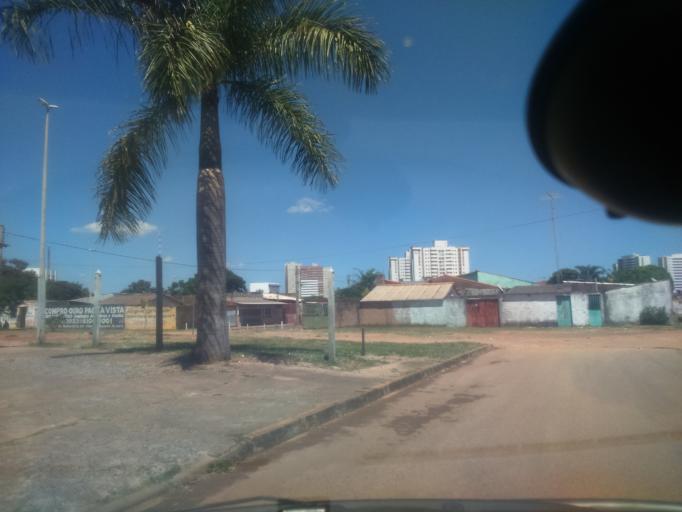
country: BR
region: Federal District
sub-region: Brasilia
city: Brasilia
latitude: -15.9984
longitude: -48.0536
